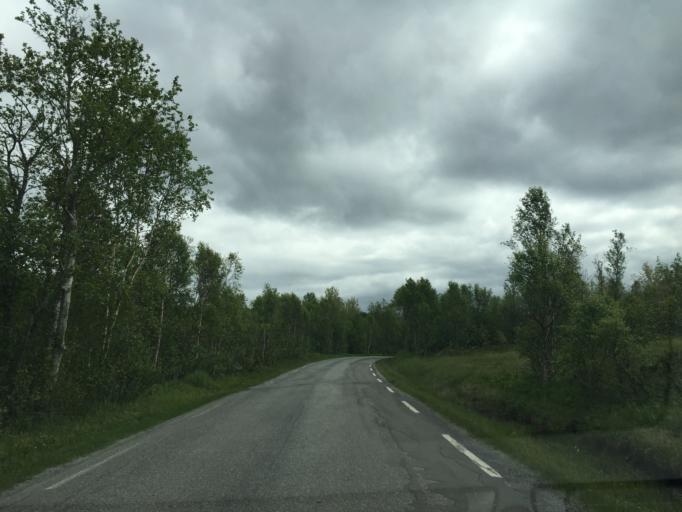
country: NO
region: Nordland
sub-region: Bodo
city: Loding
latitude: 67.3131
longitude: 14.6400
